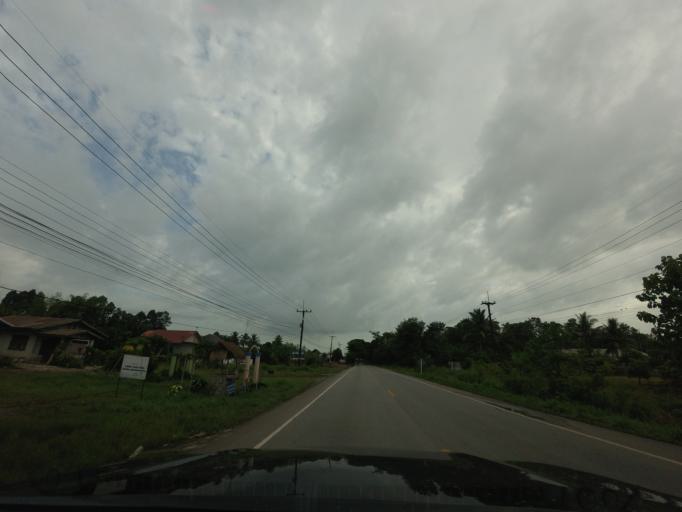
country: TH
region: Changwat Udon Thani
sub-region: Amphoe Ban Phue
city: Ban Phue
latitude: 17.7263
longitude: 102.3948
